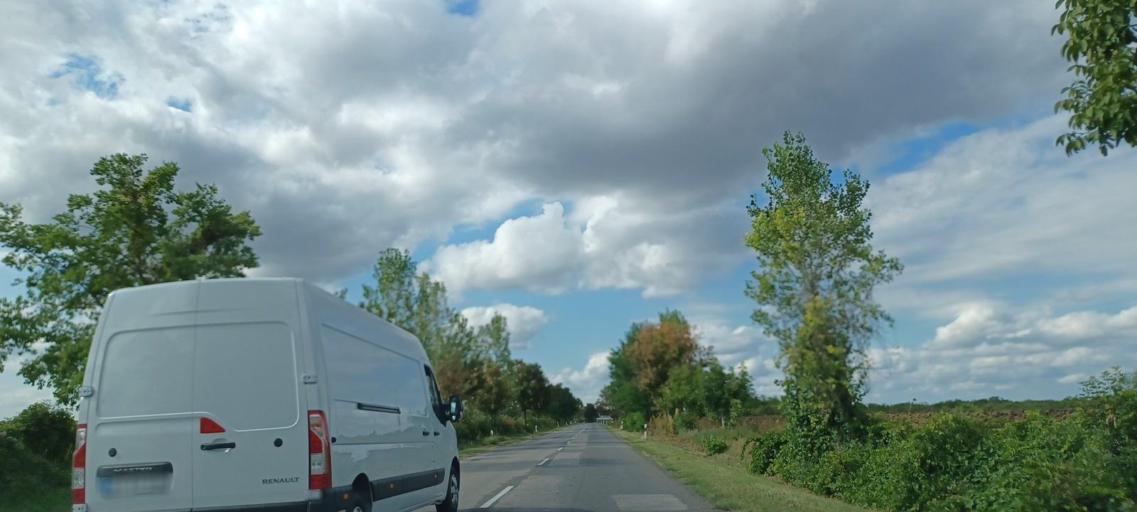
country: HU
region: Tolna
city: Szentgalpuszta
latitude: 46.3916
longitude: 18.6254
